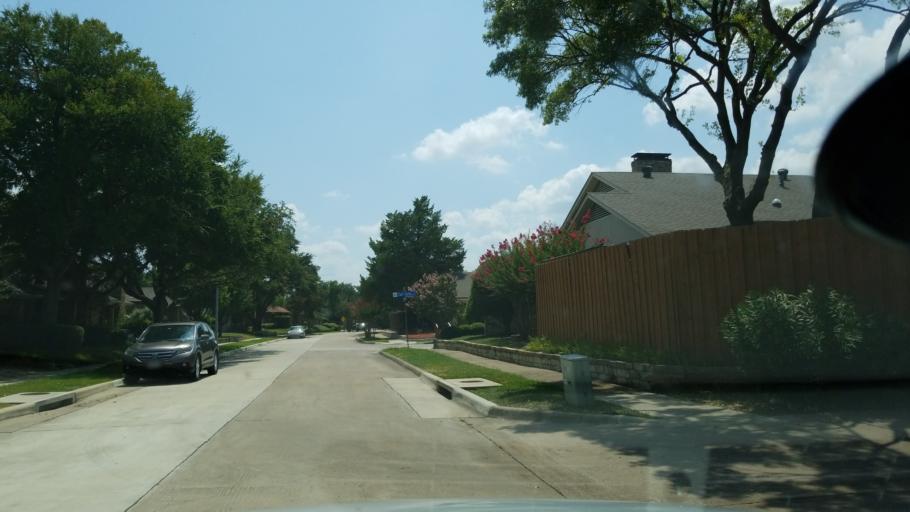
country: US
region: Texas
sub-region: Dallas County
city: Richardson
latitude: 32.9278
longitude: -96.7300
